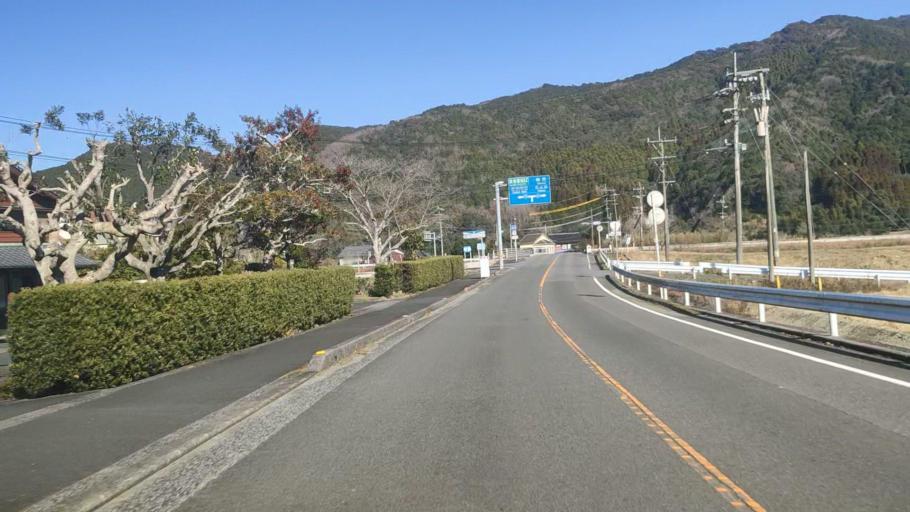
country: JP
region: Oita
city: Saiki
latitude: 32.9309
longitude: 131.9217
